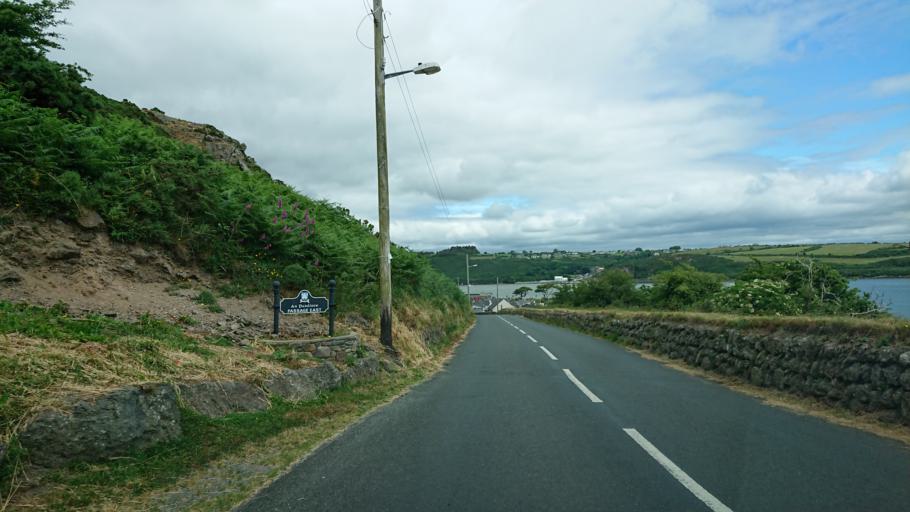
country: IE
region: Munster
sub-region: Waterford
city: Dunmore East
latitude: 52.2355
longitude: -6.9721
